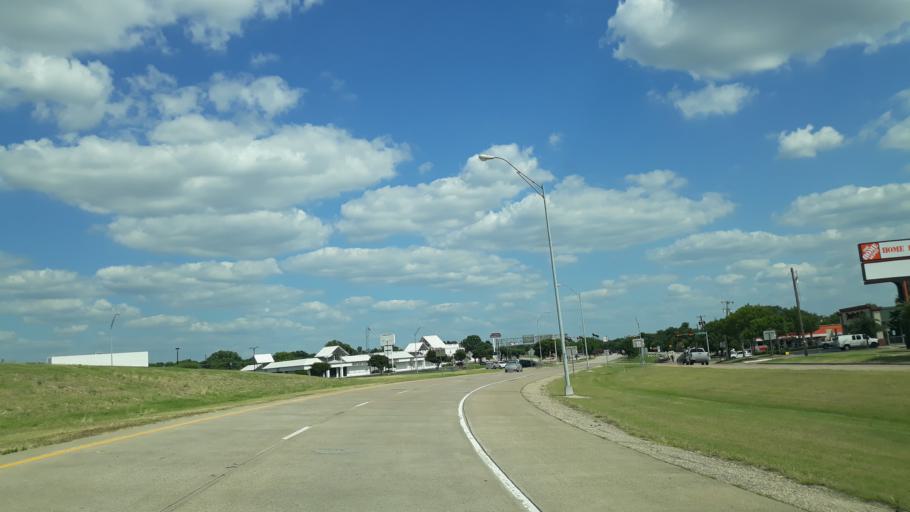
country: US
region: Texas
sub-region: Dallas County
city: Irving
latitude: 32.8350
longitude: -96.9899
